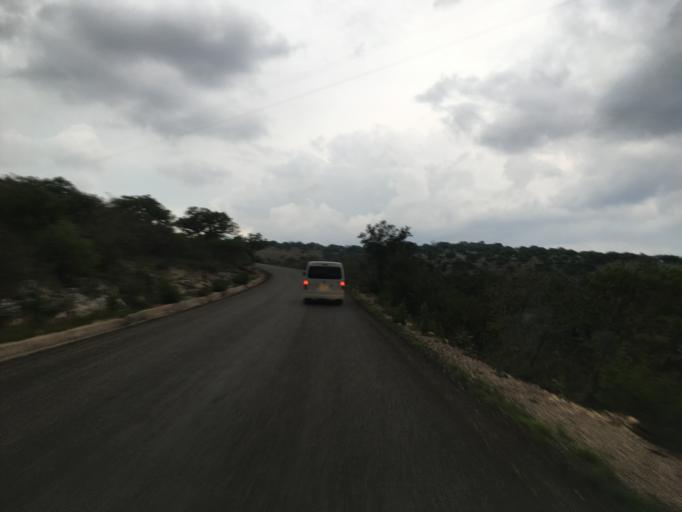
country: MX
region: Oaxaca
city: Magdalena Jaltepec
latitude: 17.2962
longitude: -97.2731
